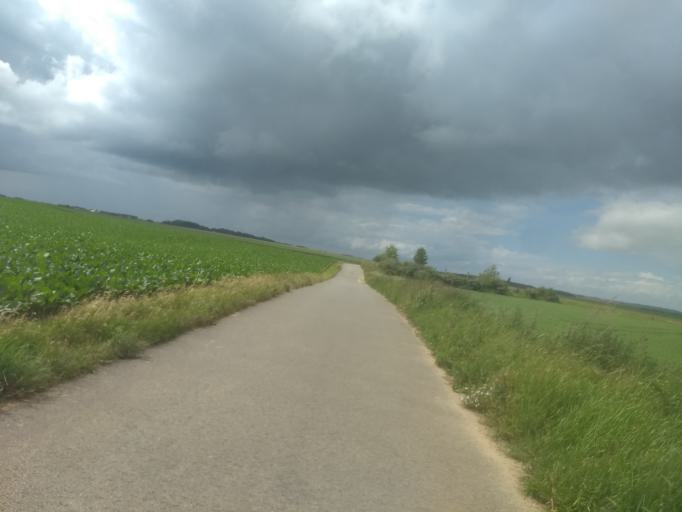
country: FR
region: Nord-Pas-de-Calais
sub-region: Departement du Pas-de-Calais
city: Dainville
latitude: 50.2604
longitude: 2.7081
